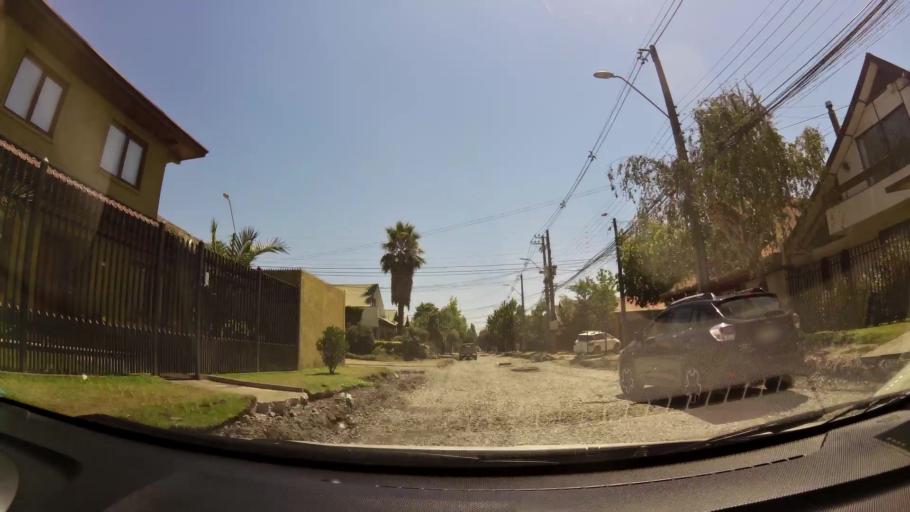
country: CL
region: Maule
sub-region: Provincia de Curico
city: Curico
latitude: -34.9788
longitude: -71.2199
